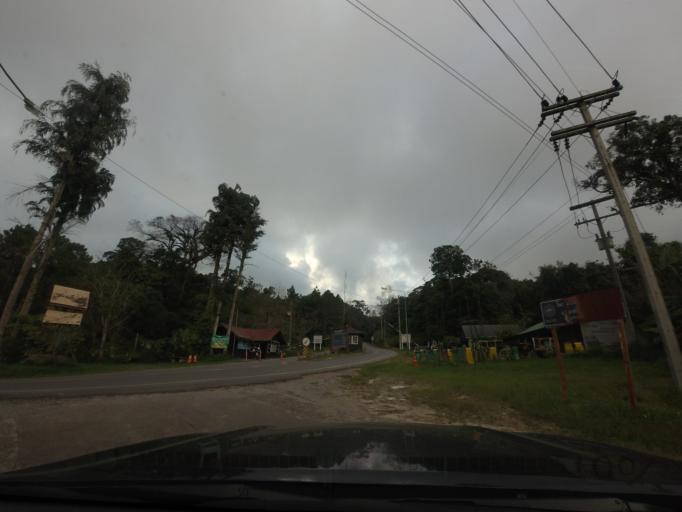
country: TH
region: Phetchabun
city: Lom Kao
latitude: 16.8938
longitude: 101.0993
